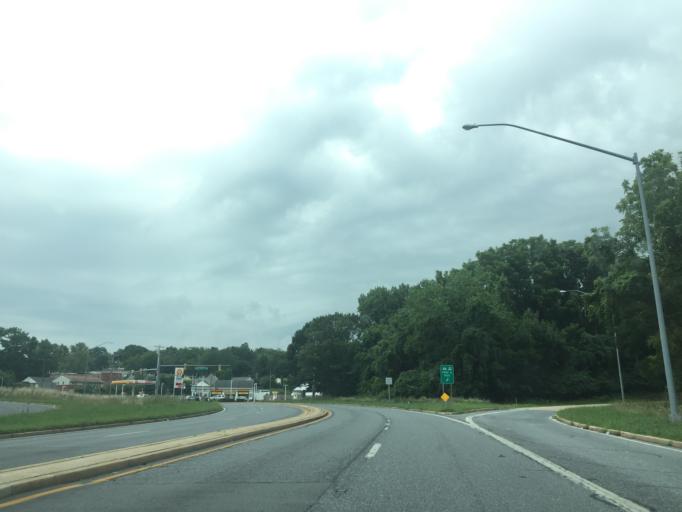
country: US
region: Maryland
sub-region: Baltimore County
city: Woodlawn
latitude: 39.3008
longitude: -76.7122
